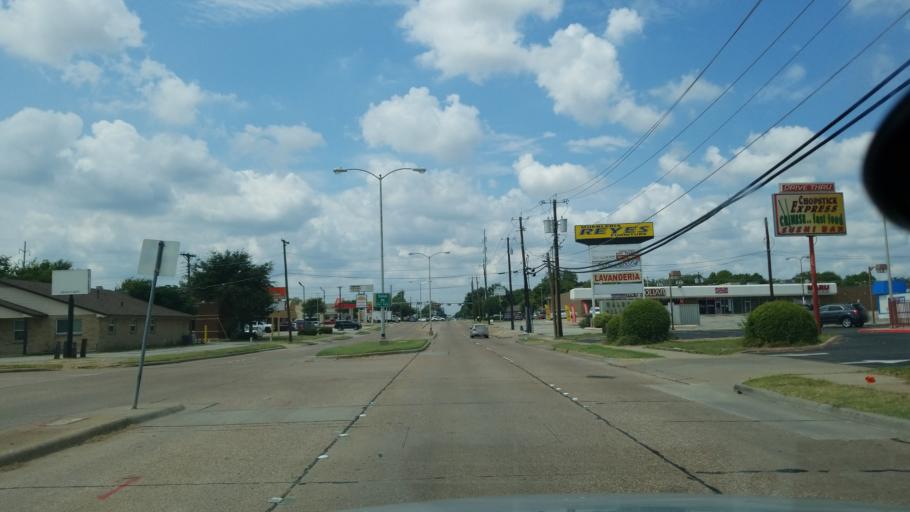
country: US
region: Texas
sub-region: Dallas County
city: Garland
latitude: 32.9164
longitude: -96.6628
